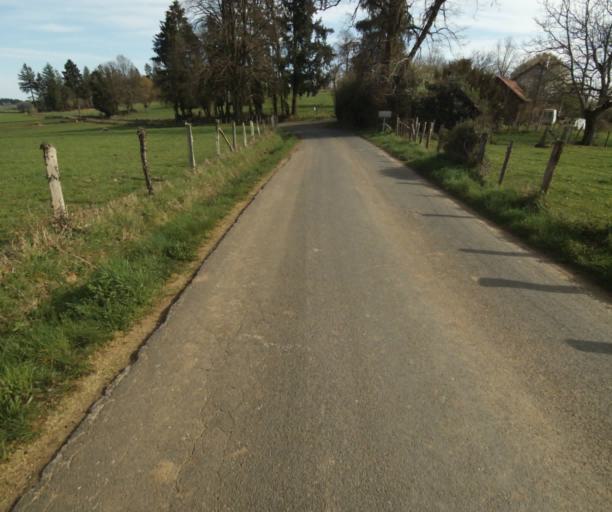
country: FR
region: Limousin
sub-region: Departement de la Correze
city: Seilhac
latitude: 45.3325
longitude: 1.7237
